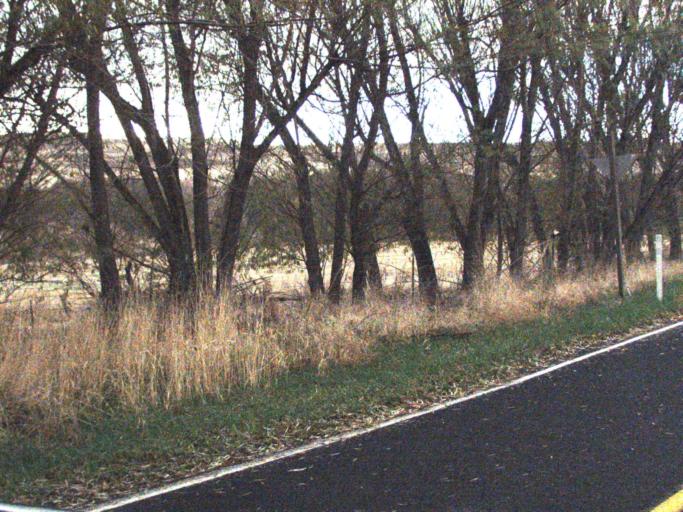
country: US
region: Washington
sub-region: Walla Walla County
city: Waitsburg
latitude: 46.5274
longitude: -118.1398
